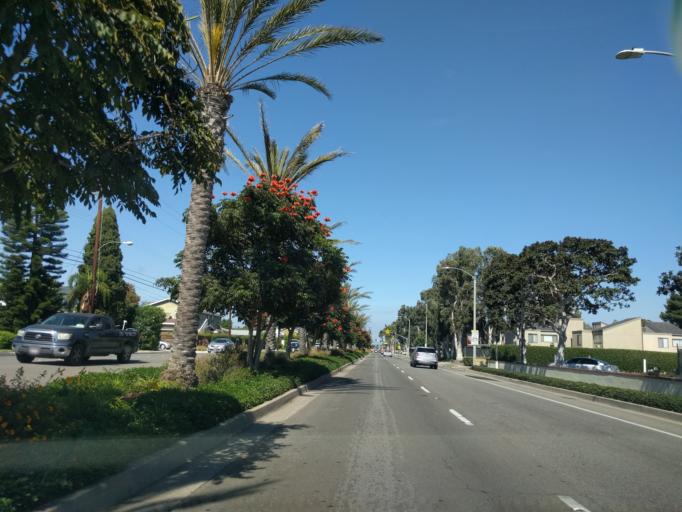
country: US
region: California
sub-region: Orange County
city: Costa Mesa
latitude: 33.6296
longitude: -117.9074
